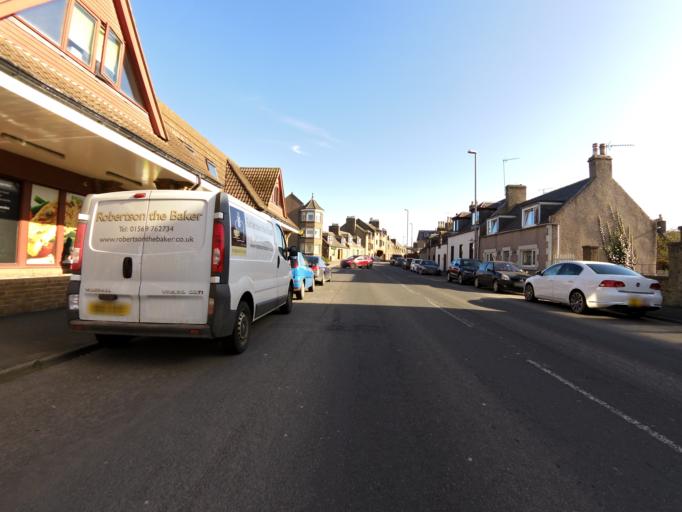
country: GB
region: Scotland
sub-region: Aberdeenshire
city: Stonehaven
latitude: 56.9664
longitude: -2.2088
